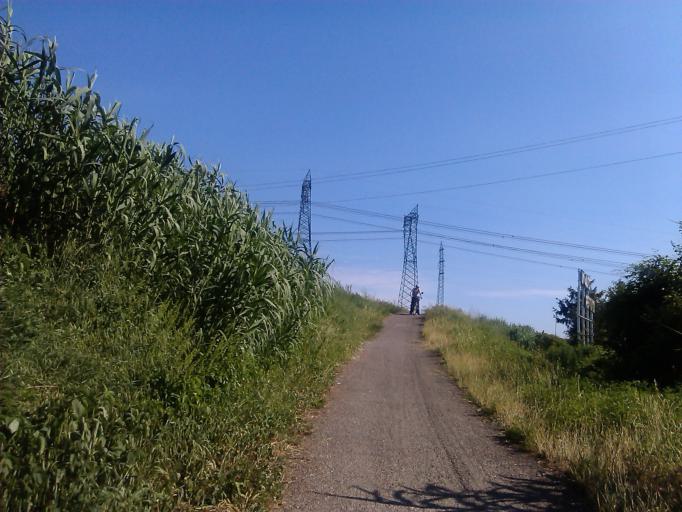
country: IT
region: Tuscany
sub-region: Province of Florence
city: Campi Bisenzio
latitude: 43.8535
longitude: 11.1243
